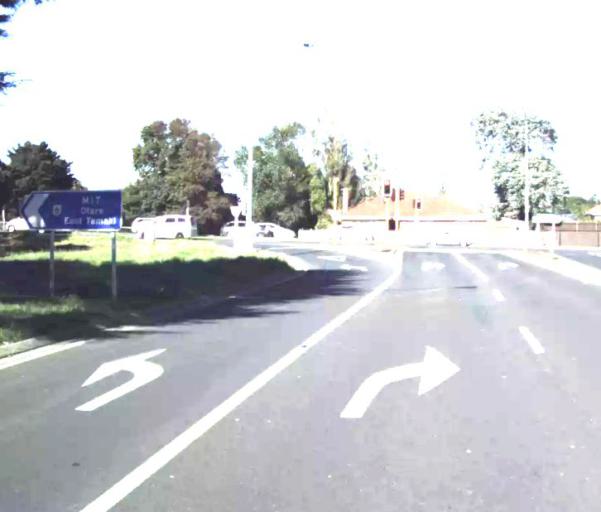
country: NZ
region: Auckland
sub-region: Auckland
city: Manukau City
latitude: -36.9639
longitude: 174.8666
